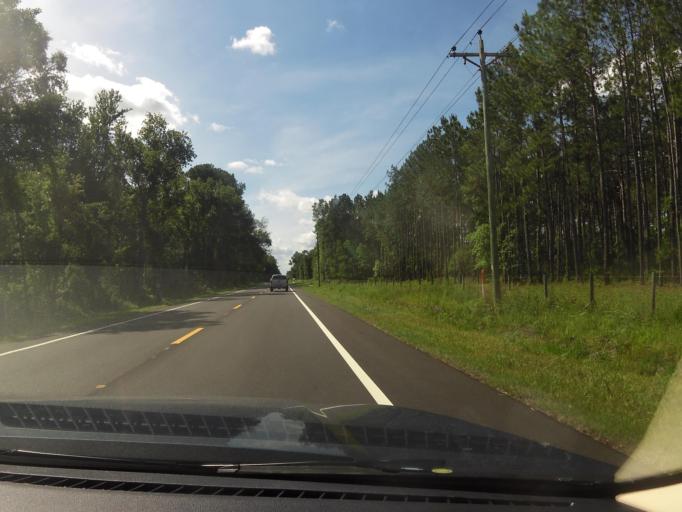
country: US
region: Florida
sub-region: Nassau County
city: Callahan
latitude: 30.6090
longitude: -81.8741
